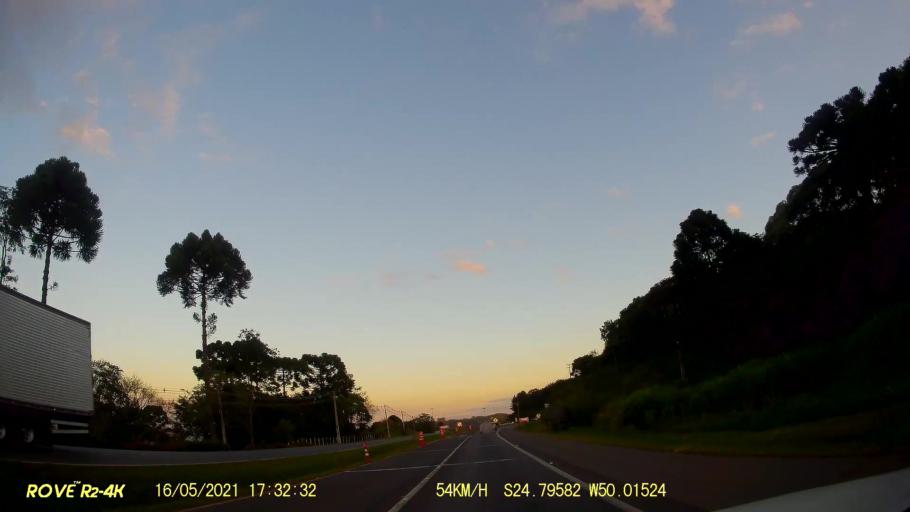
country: BR
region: Parana
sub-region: Castro
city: Castro
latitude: -24.7960
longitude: -50.0152
